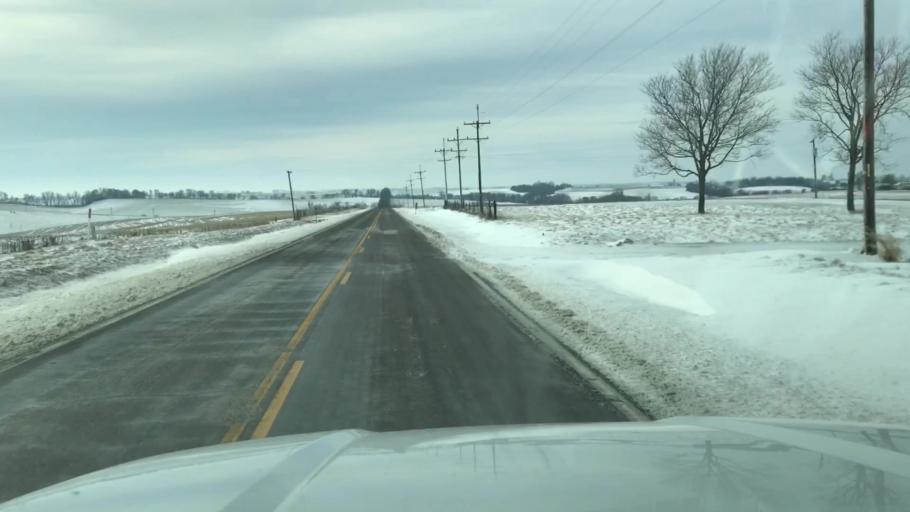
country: US
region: Missouri
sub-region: Holt County
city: Mound City
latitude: 40.1022
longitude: -95.1449
